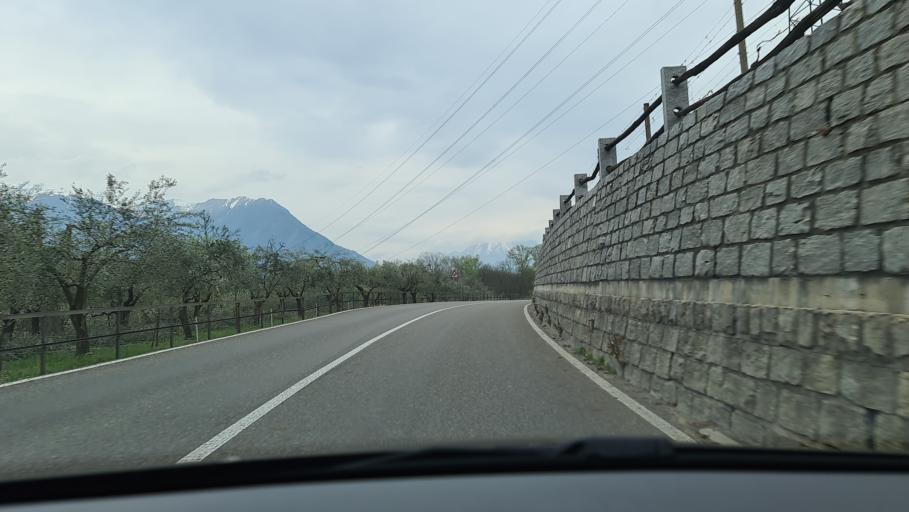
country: CH
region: Ticino
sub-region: Bellinzona District
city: Sementina
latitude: 46.1770
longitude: 8.9680
